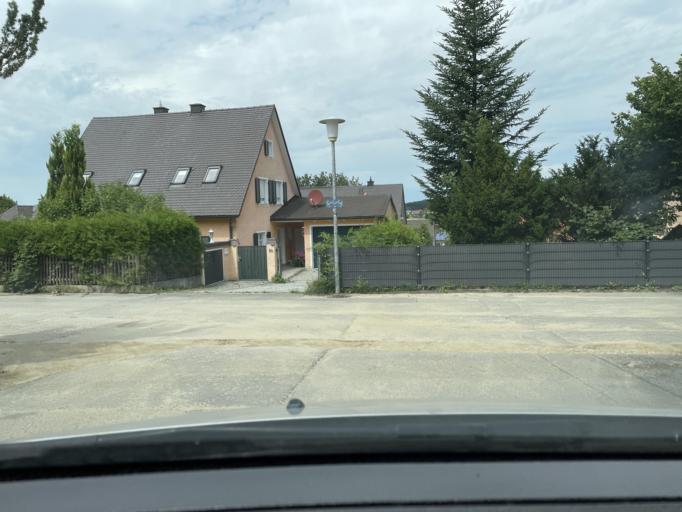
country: DE
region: Bavaria
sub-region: Lower Bavaria
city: Altfraunhofen
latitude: 48.4481
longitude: 12.1731
